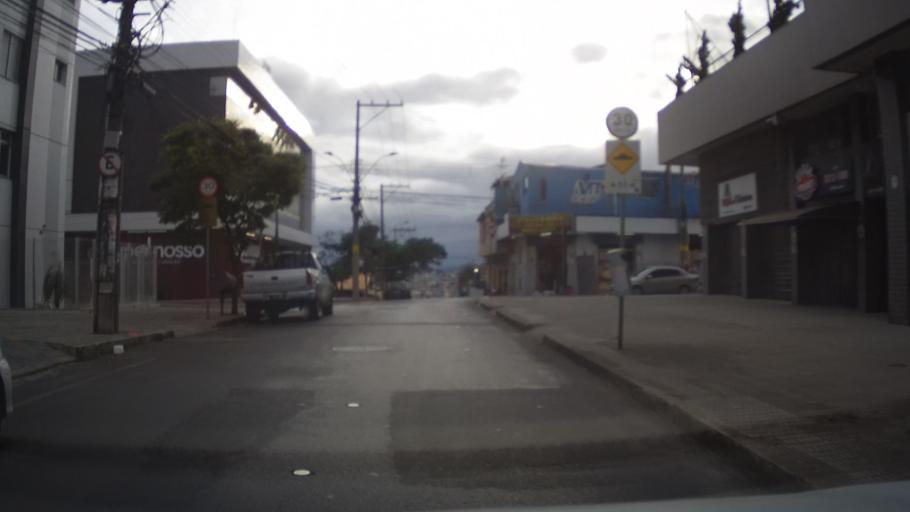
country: BR
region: Minas Gerais
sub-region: Belo Horizonte
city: Belo Horizonte
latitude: -19.9064
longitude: -43.9718
